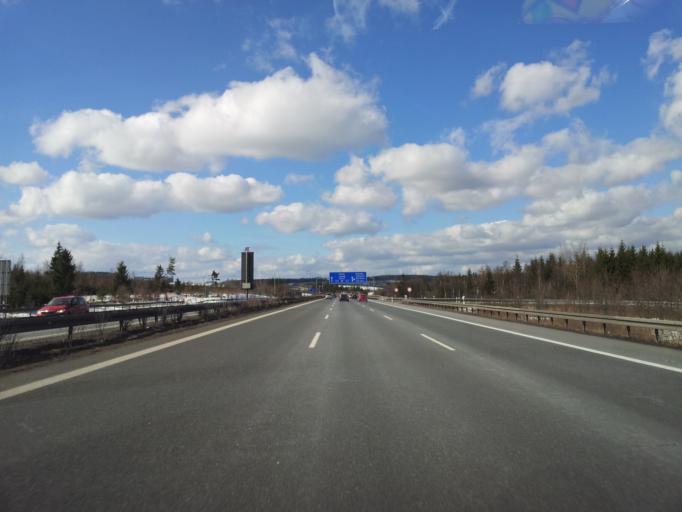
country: DE
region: Bavaria
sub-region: Upper Franconia
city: Leupoldsgrun
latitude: 50.3119
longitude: 11.8010
